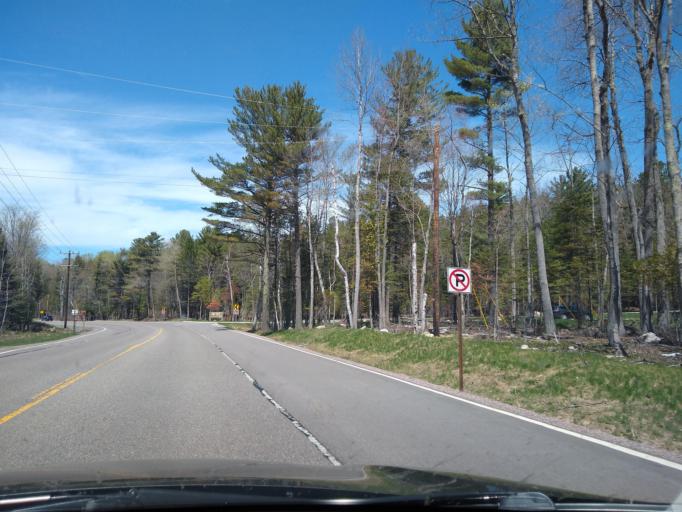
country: US
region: Michigan
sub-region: Marquette County
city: Trowbridge Park
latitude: 46.6004
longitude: -87.4576
